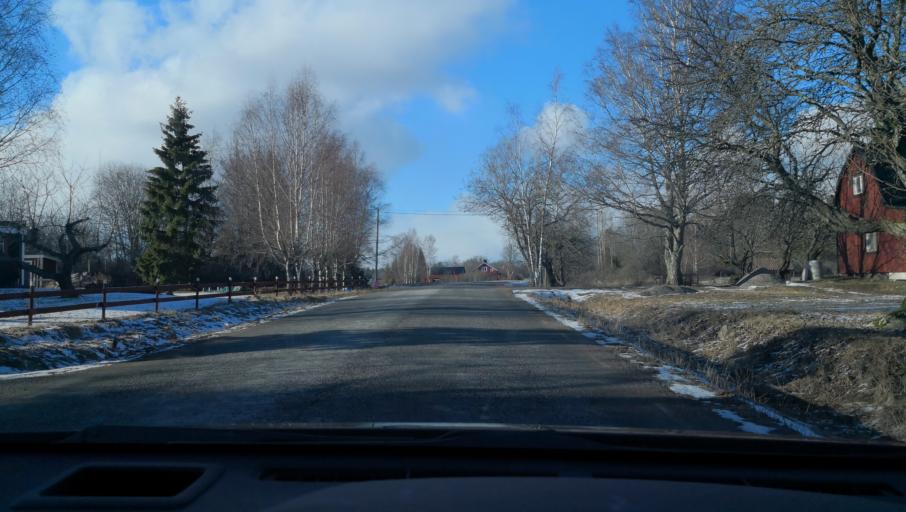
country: SE
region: Uppsala
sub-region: Enkopings Kommun
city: Hummelsta
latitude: 59.6356
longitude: 16.9721
